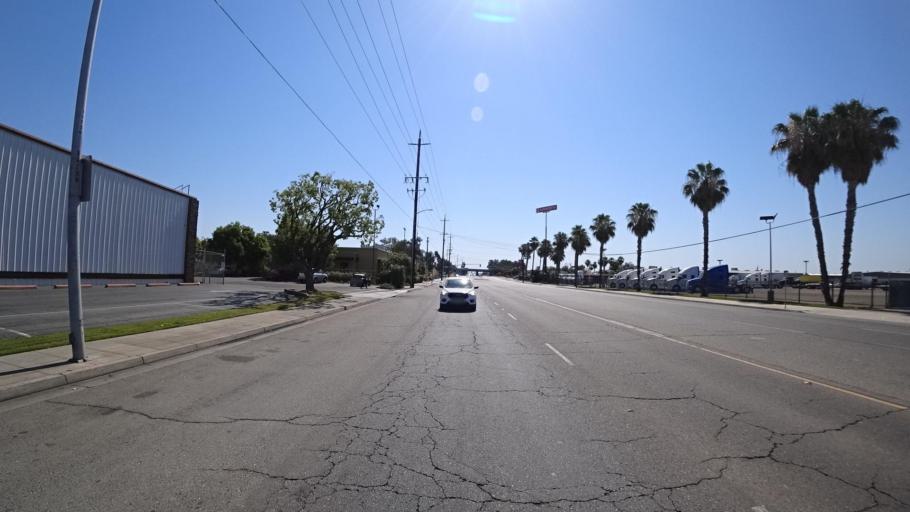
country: US
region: California
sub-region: Fresno County
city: Fresno
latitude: 36.7070
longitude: -119.7784
